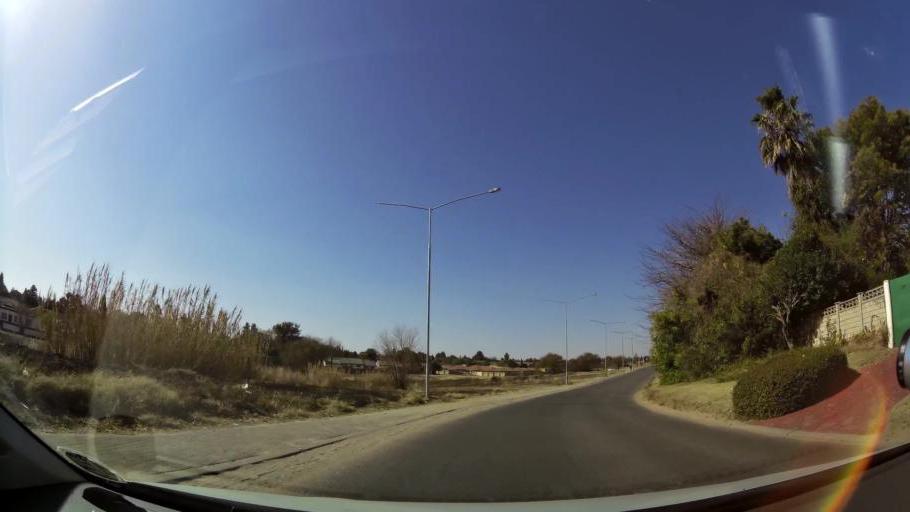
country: ZA
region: Gauteng
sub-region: Ekurhuleni Metropolitan Municipality
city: Tembisa
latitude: -26.0391
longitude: 28.2246
